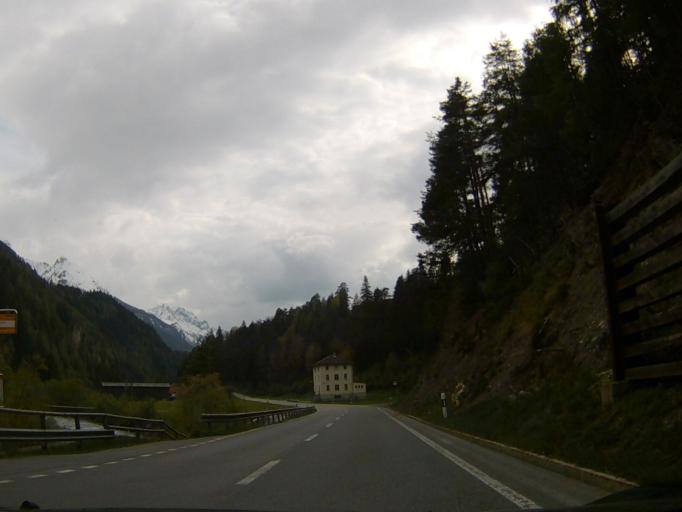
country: AT
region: Tyrol
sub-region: Politischer Bezirk Landeck
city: Nauders
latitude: 46.8721
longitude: 10.4482
